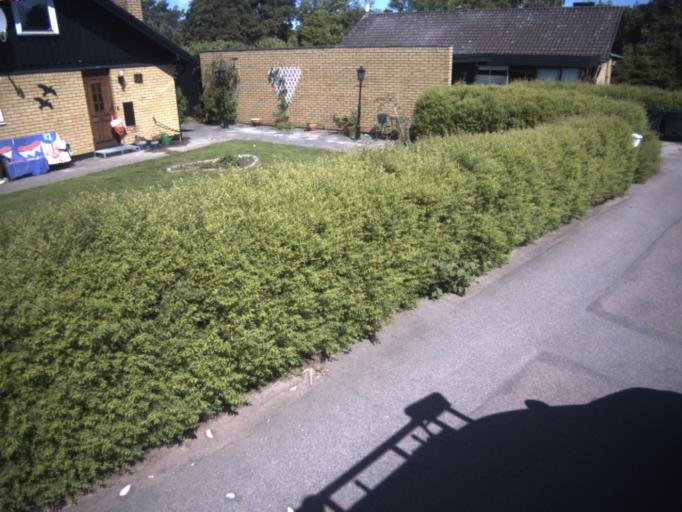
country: SE
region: Skane
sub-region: Helsingborg
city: Gantofta
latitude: 55.9906
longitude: 12.8013
